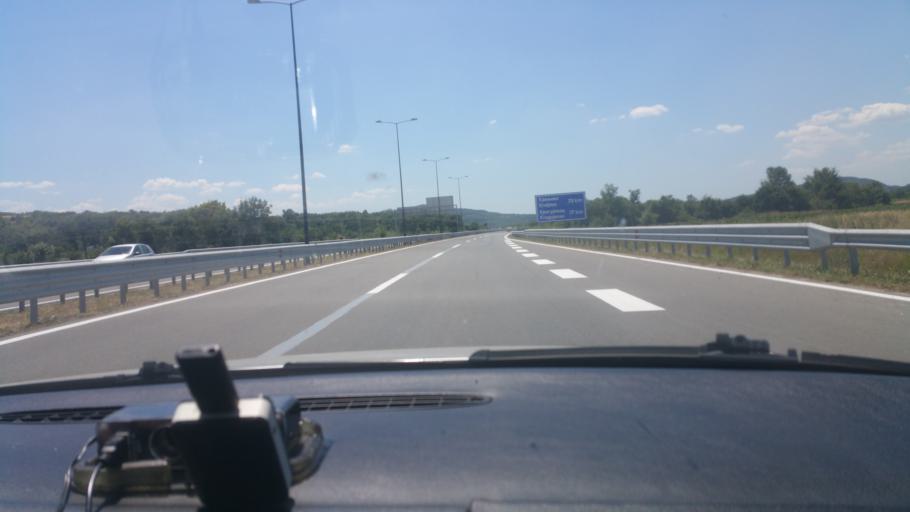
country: RS
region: Central Serbia
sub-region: Sumadijski Okrug
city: Batocina
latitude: 44.1423
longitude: 21.0275
